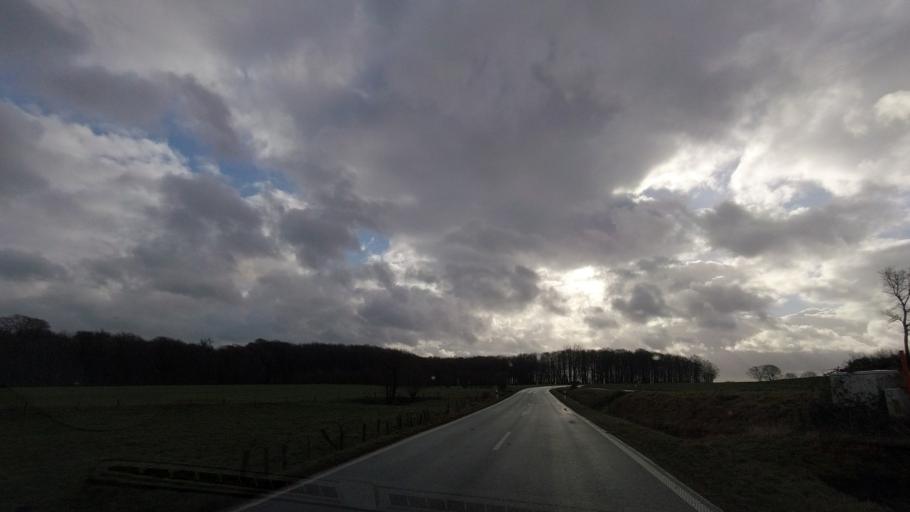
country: DE
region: Schleswig-Holstein
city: Grodersby
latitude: 54.6531
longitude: 9.9118
